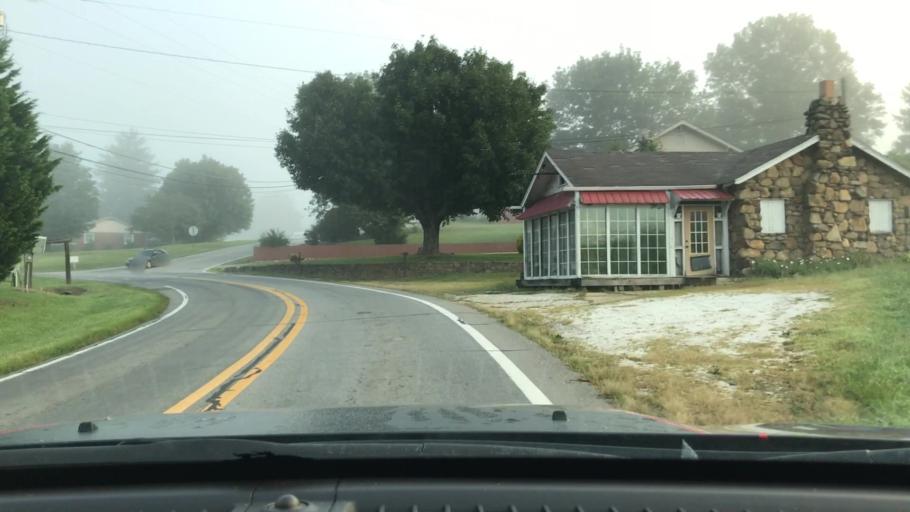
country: US
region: North Carolina
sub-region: Buncombe County
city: Woodfin
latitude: 35.6260
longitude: -82.6132
